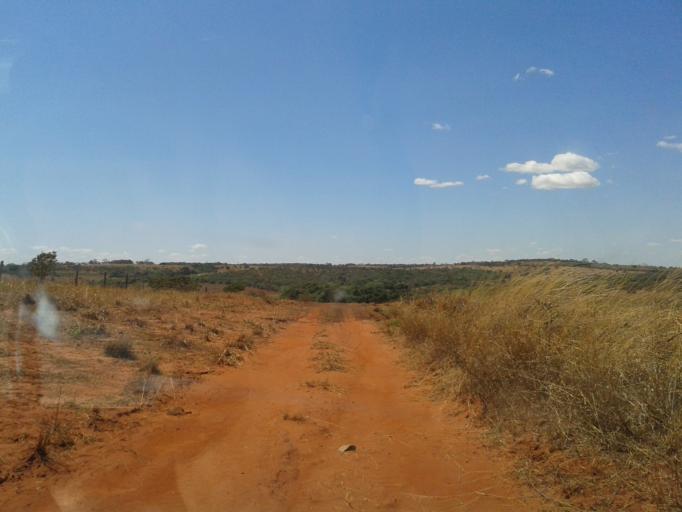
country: BR
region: Minas Gerais
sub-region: Monte Alegre De Minas
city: Monte Alegre de Minas
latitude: -18.8026
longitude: -49.0805
